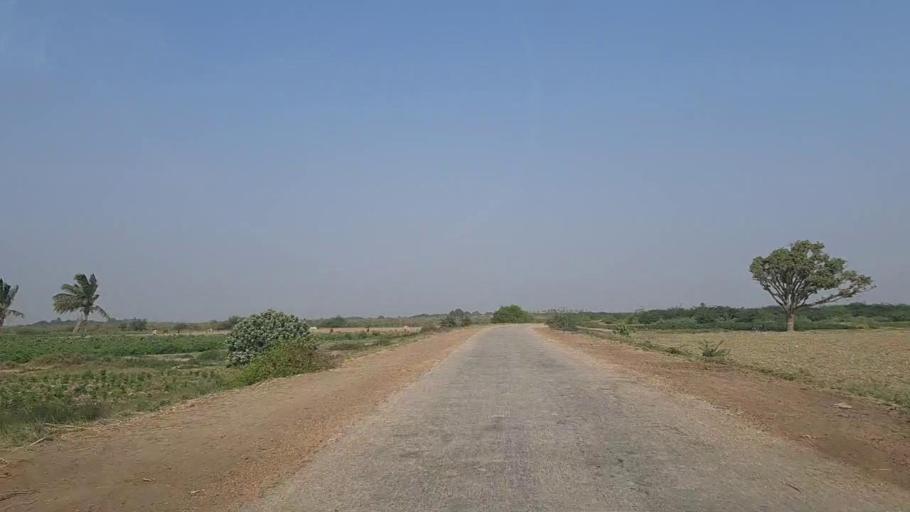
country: PK
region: Sindh
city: Keti Bandar
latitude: 24.2448
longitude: 67.7090
